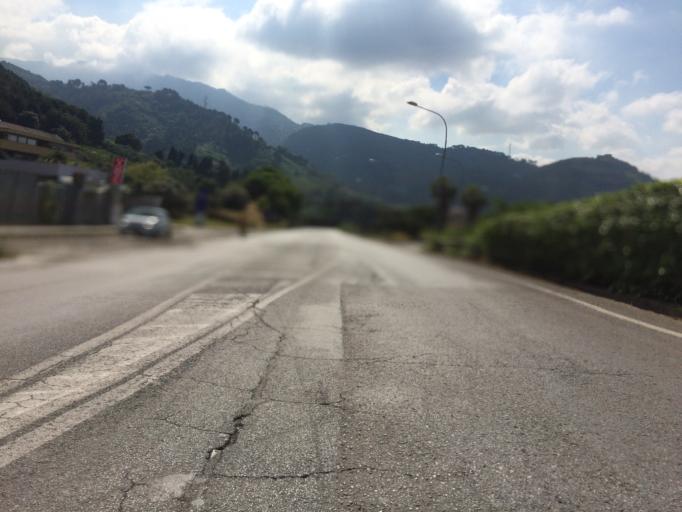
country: IT
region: Tuscany
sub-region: Provincia di Massa-Carrara
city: San Vito-Cerreto
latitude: 44.0186
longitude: 10.1519
